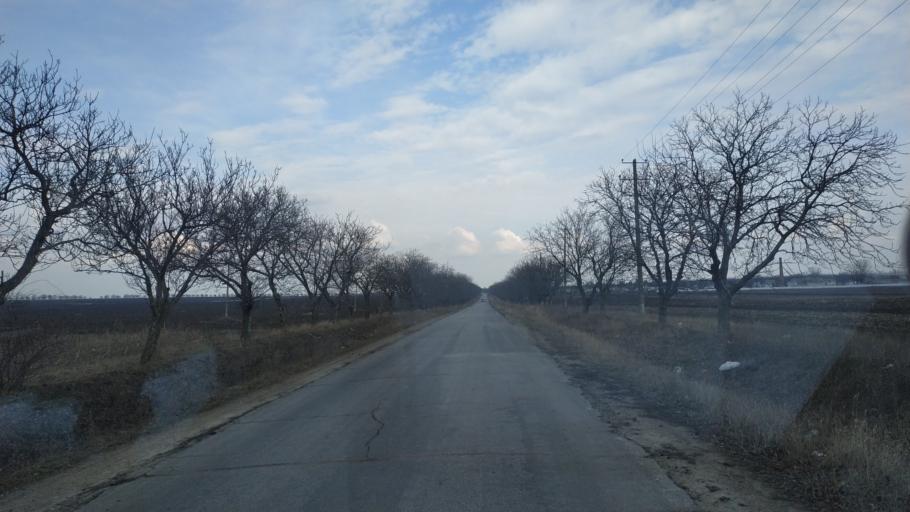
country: MD
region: Anenii Noi
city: Anenii Noi
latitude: 46.9103
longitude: 29.3258
